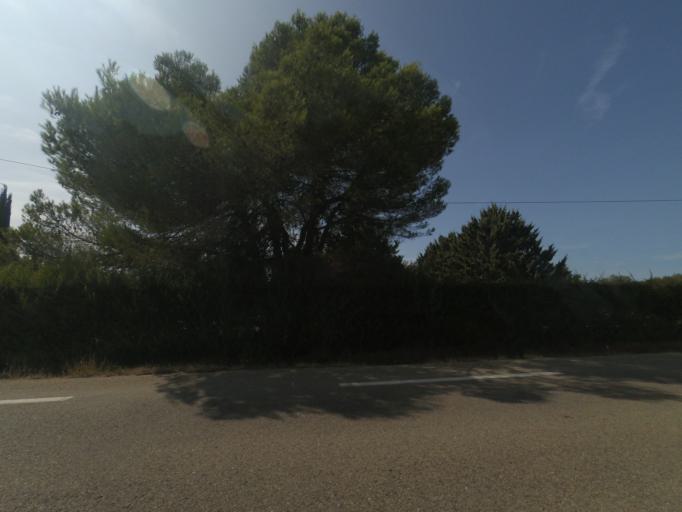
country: FR
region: Languedoc-Roussillon
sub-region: Departement du Gard
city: Villevieille
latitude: 43.8282
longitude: 4.1330
